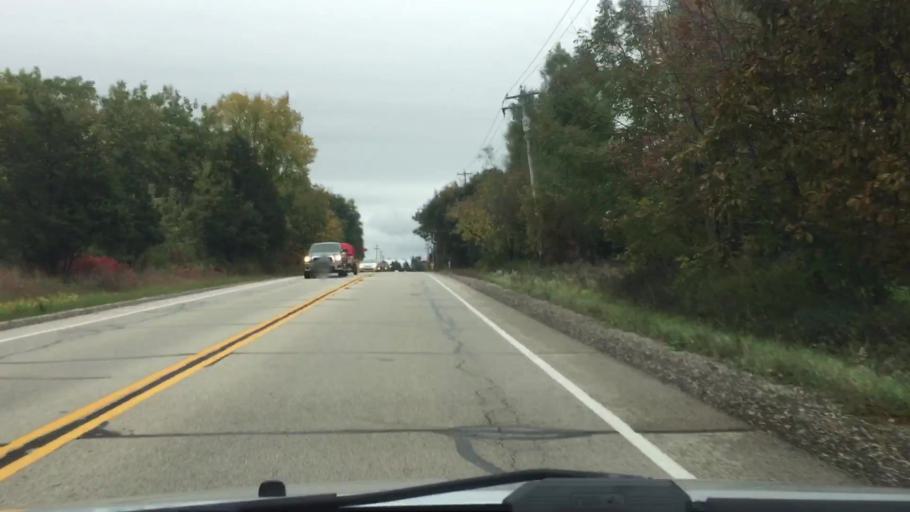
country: US
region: Wisconsin
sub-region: Jefferson County
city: Palmyra
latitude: 42.7834
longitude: -88.5582
